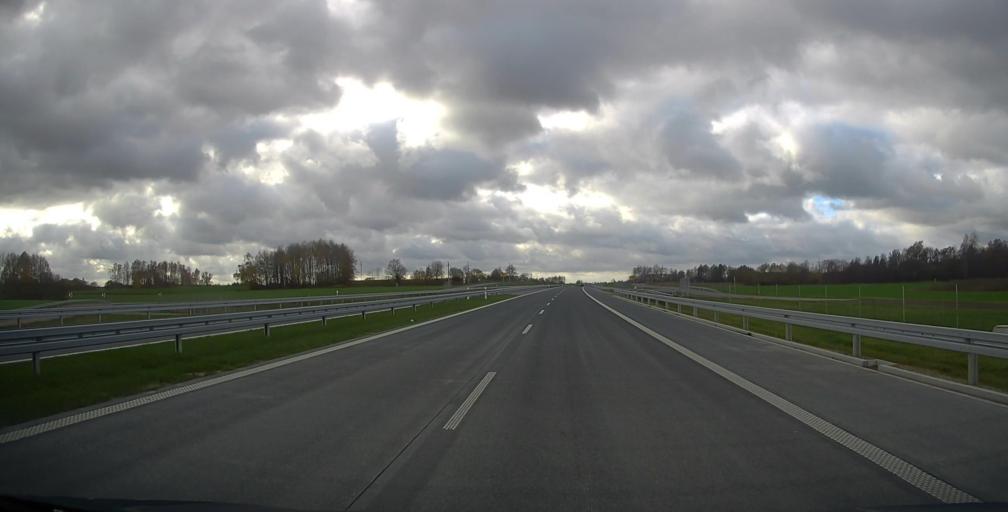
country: PL
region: Podlasie
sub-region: Powiat suwalski
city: Raczki
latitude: 53.9183
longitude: 22.7392
